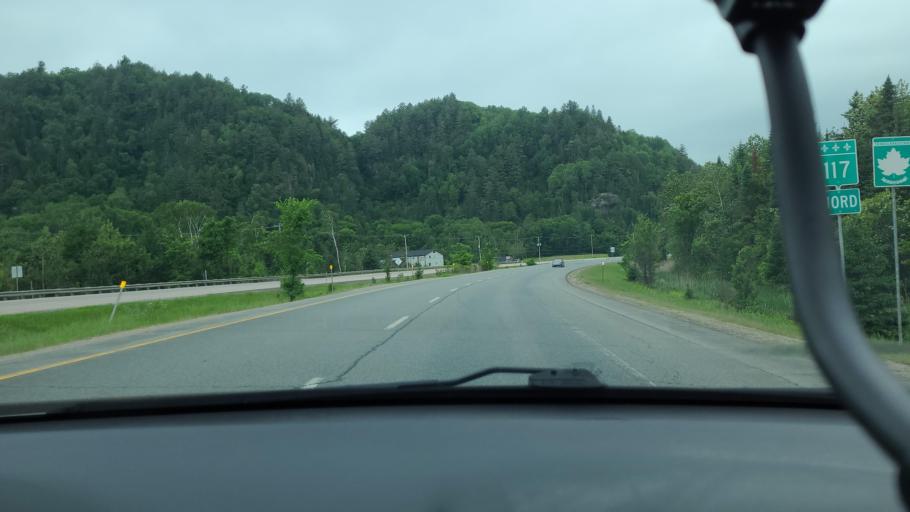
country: CA
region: Quebec
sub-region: Laurentides
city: Mont-Tremblant
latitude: 46.1573
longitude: -74.7013
